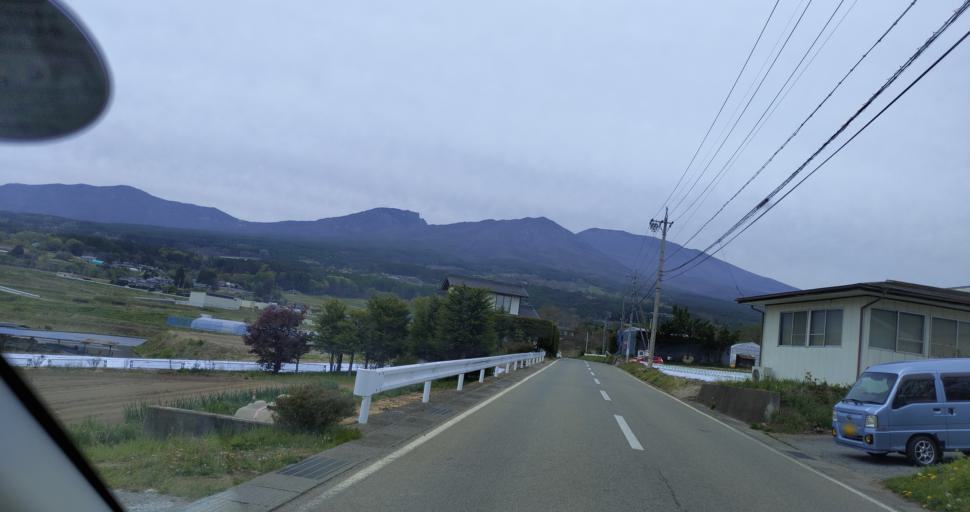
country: JP
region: Nagano
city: Komoro
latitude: 36.3308
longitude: 138.4891
